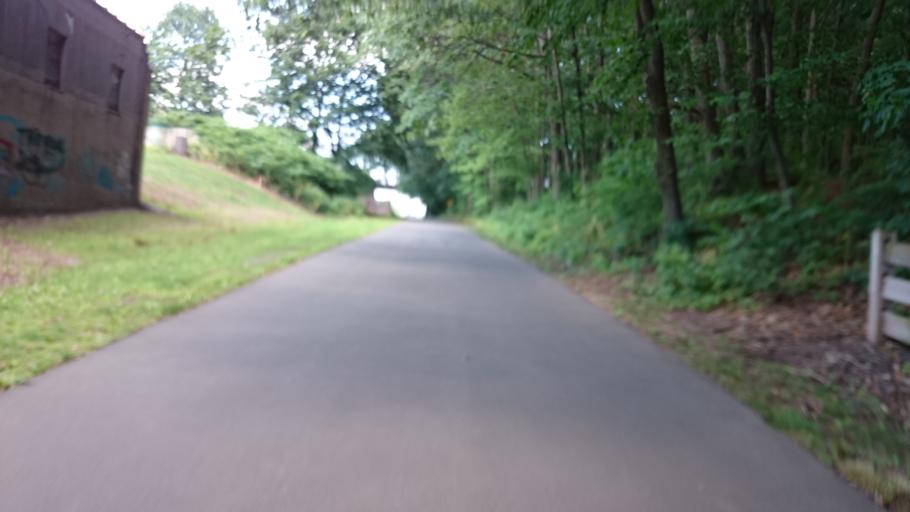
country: US
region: Connecticut
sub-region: New Haven County
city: New Haven
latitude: 41.3520
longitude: -72.9278
